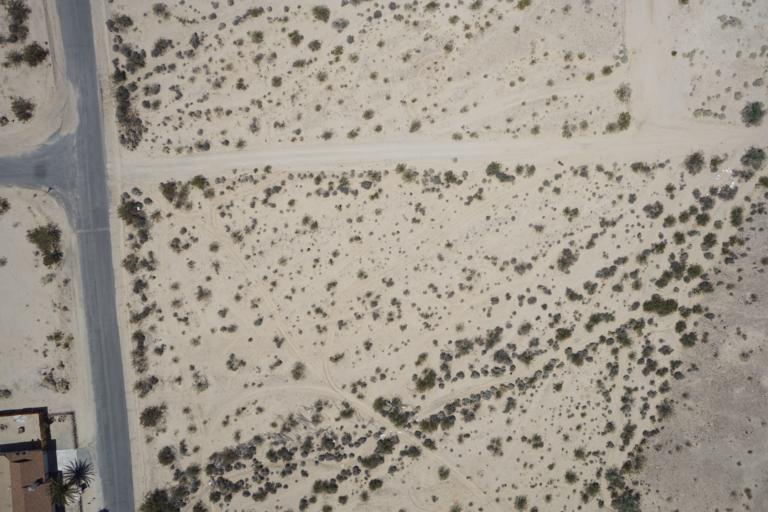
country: US
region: California
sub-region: San Bernardino County
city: Twentynine Palms
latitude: 34.1328
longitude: -116.0320
